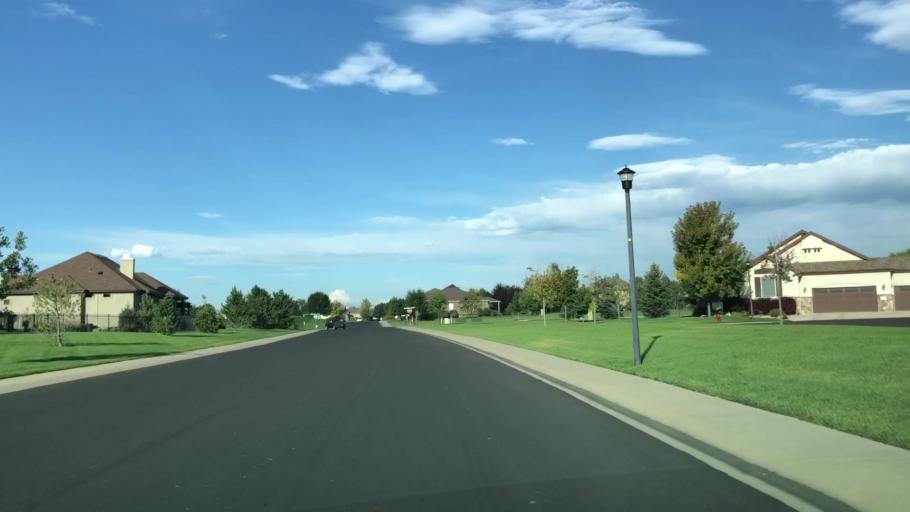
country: US
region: Colorado
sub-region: Weld County
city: Windsor
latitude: 40.4615
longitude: -104.9749
